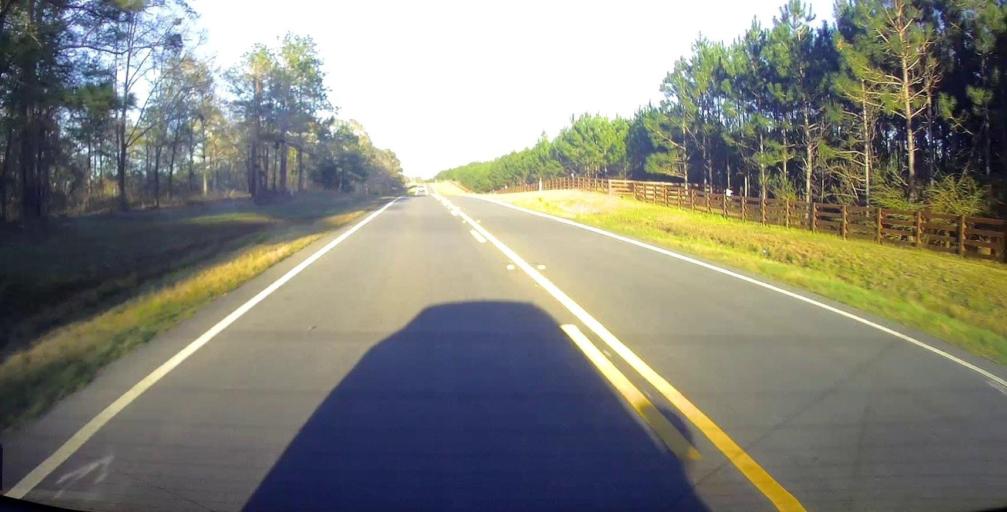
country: US
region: Georgia
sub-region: Wilcox County
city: Abbeville
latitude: 31.9871
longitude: -83.3359
